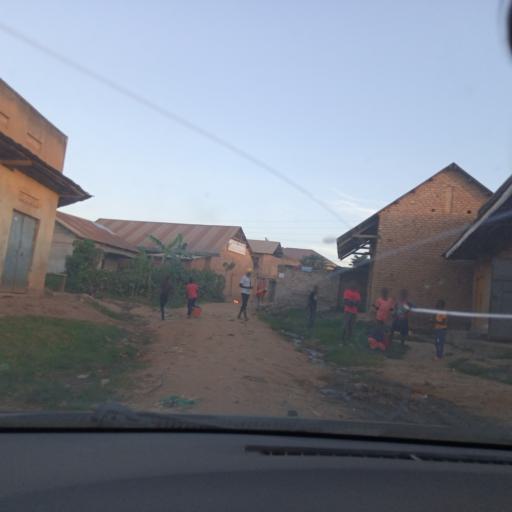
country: UG
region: Central Region
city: Masaka
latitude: -0.3227
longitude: 31.7589
